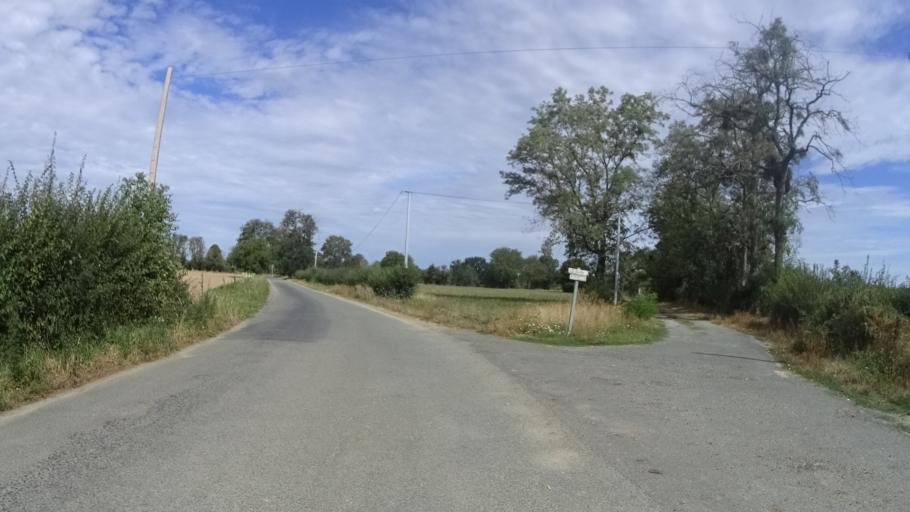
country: FR
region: Auvergne
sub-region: Departement de l'Allier
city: Beaulon
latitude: 46.6473
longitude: 3.6902
